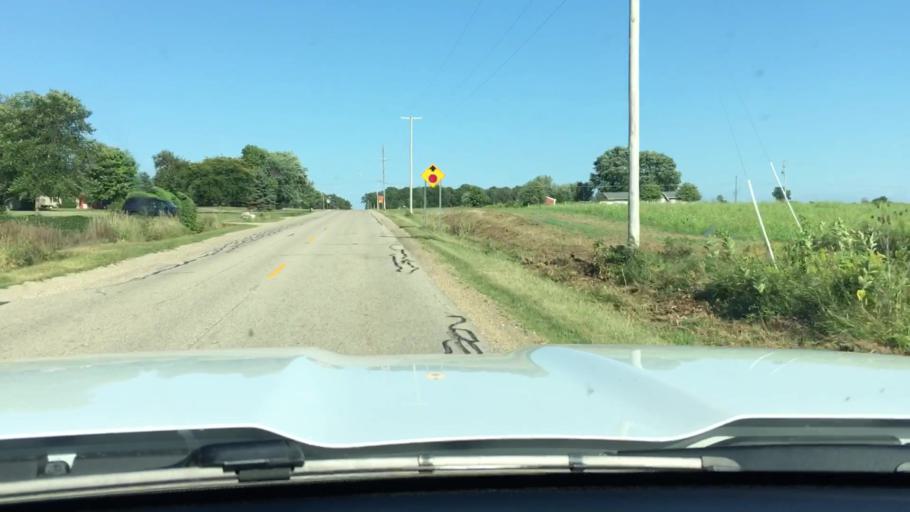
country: US
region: Michigan
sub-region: Ottawa County
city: Zeeland
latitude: 42.8264
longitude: -85.9426
